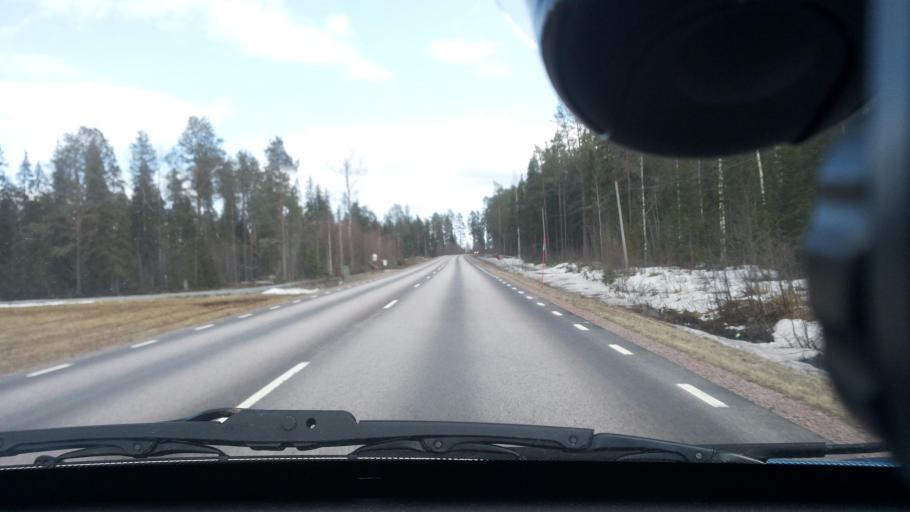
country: SE
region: Norrbotten
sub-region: Lulea Kommun
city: Gammelstad
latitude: 65.6013
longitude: 21.9821
